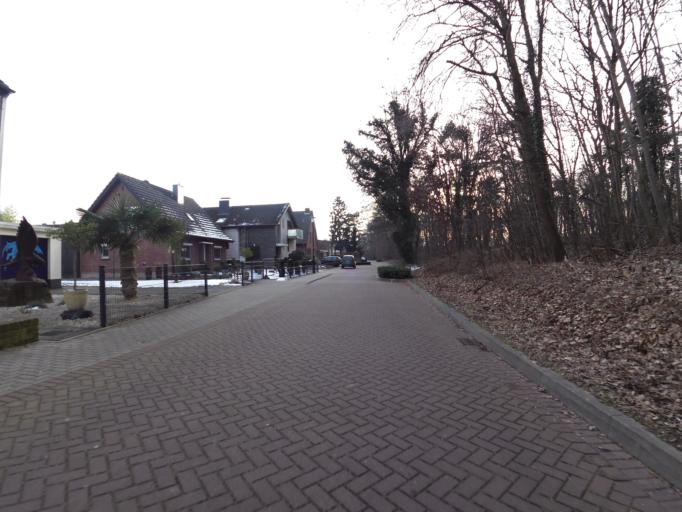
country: DE
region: North Rhine-Westphalia
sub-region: Regierungsbezirk Dusseldorf
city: Emmerich
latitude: 51.8503
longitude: 6.2532
